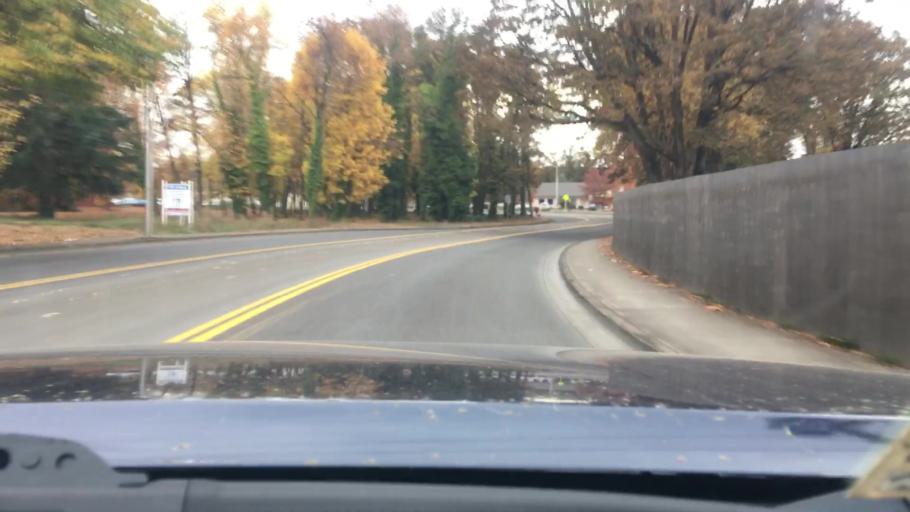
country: US
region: Oregon
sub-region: Lane County
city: Cottage Grove
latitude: 43.8004
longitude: -123.0463
